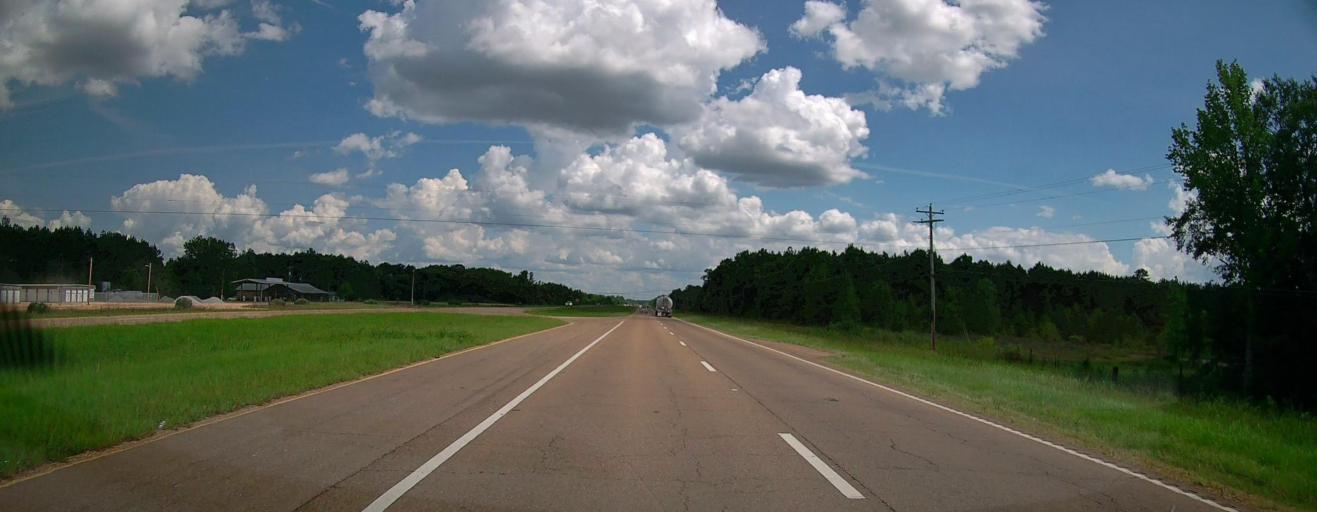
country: US
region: Mississippi
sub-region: Lowndes County
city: Columbus Air Force Base
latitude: 33.6856
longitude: -88.4360
